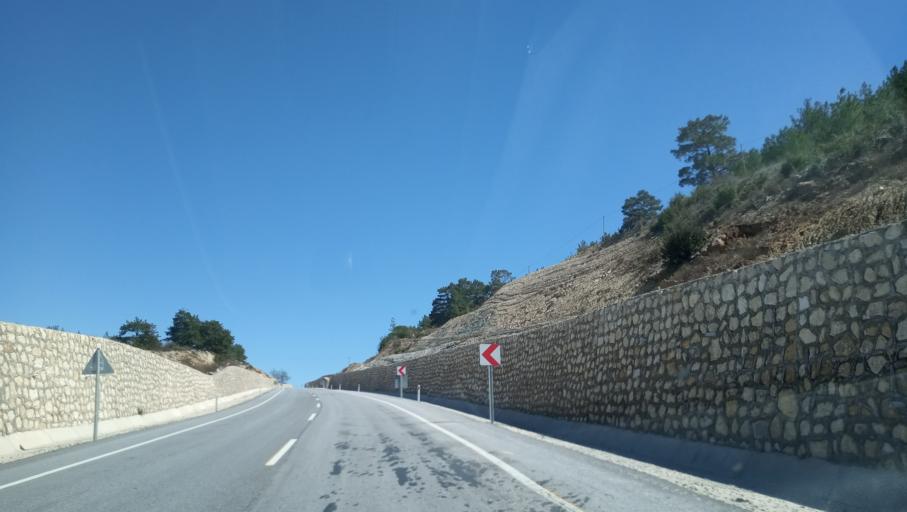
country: TR
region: Antalya
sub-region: Alanya
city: Okurcalar
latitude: 36.7749
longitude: 31.7587
